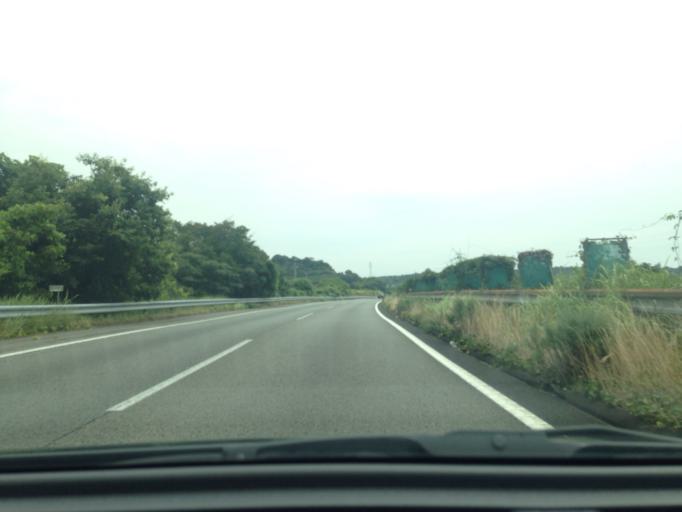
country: JP
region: Shizuoka
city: Shimada
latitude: 34.7642
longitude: 138.2082
